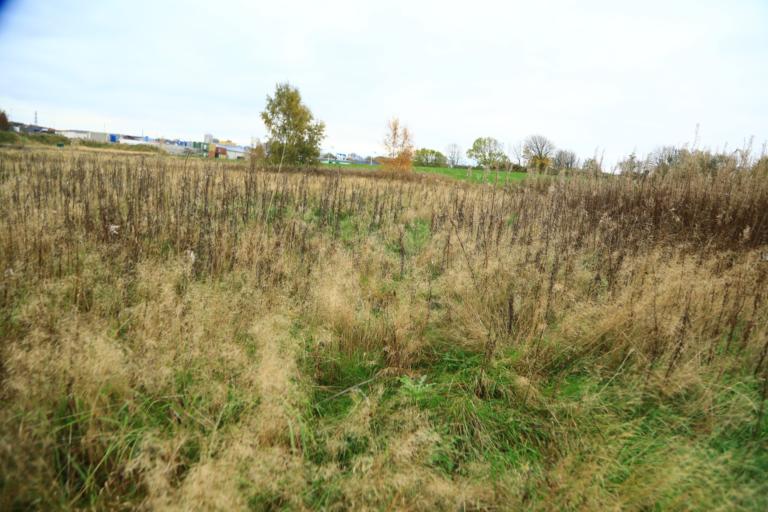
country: SE
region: Halland
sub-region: Varbergs Kommun
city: Varberg
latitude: 57.1290
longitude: 12.2785
